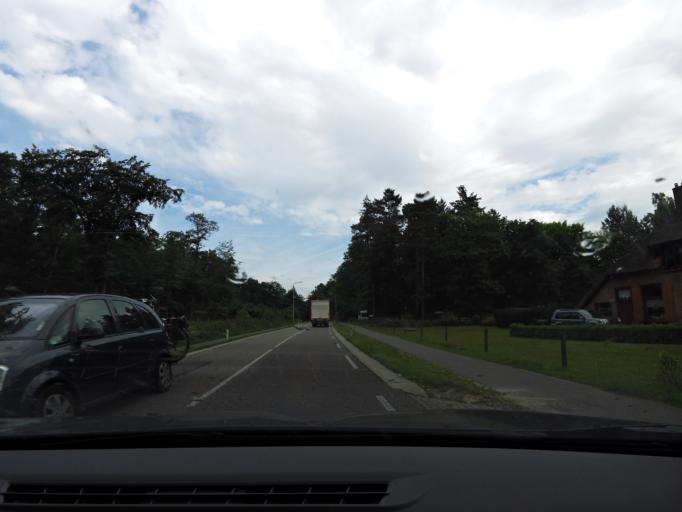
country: NL
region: Gelderland
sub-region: Gemeente Apeldoorn
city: Loenen
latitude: 52.1275
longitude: 6.0098
